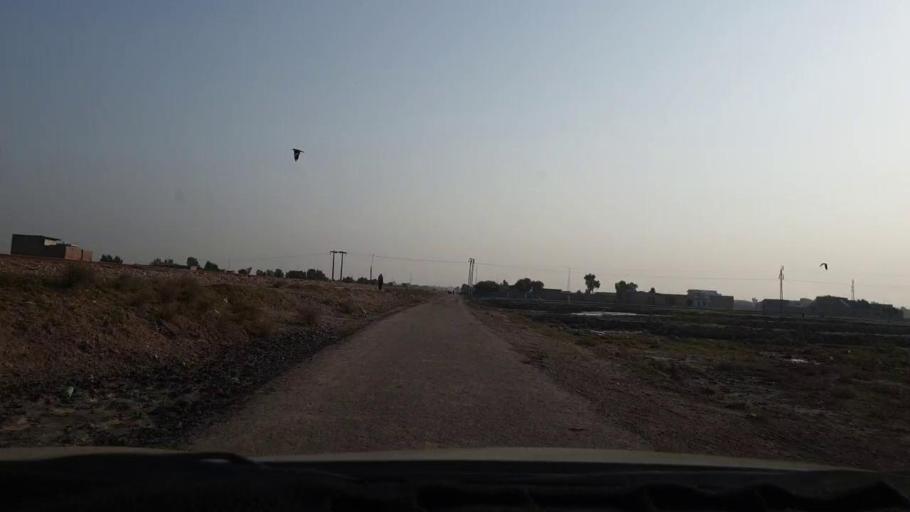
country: PK
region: Sindh
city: Larkana
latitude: 27.5269
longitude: 68.1968
